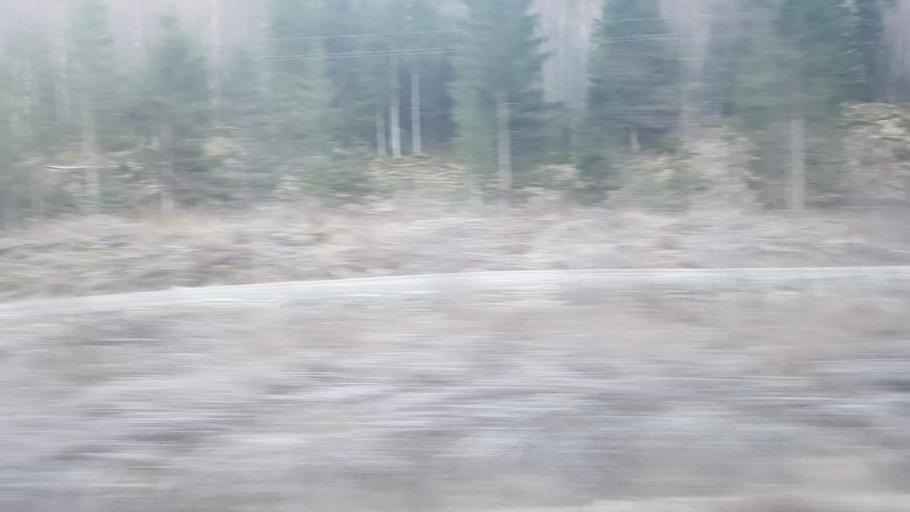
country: NO
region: Nord-Trondelag
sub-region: Stjordal
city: Stjordalshalsen
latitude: 63.5892
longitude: 11.0114
